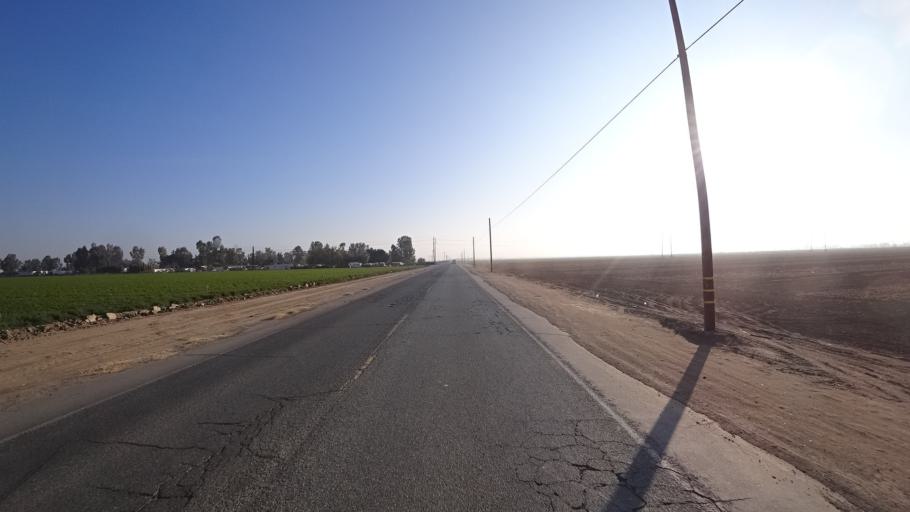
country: US
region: California
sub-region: Kern County
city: Greenfield
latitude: 35.2673
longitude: -118.9783
